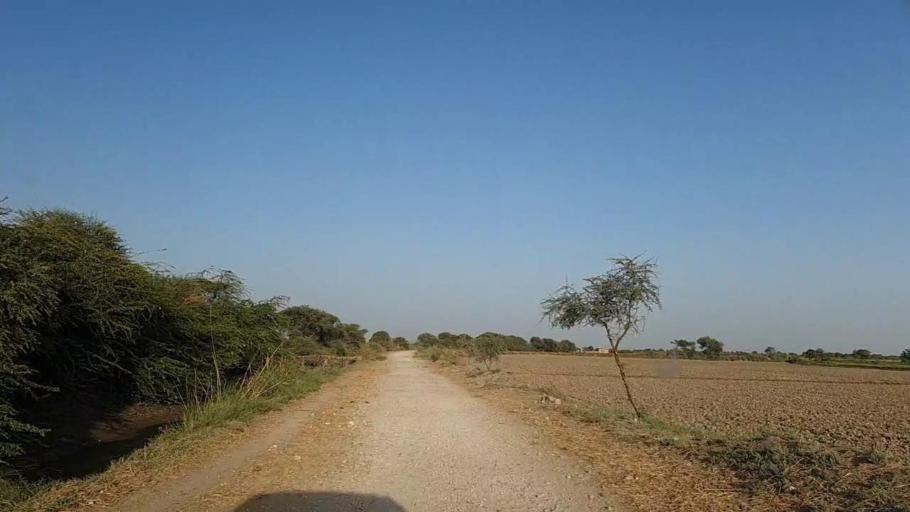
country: PK
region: Sindh
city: Jati
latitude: 24.4143
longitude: 68.3211
